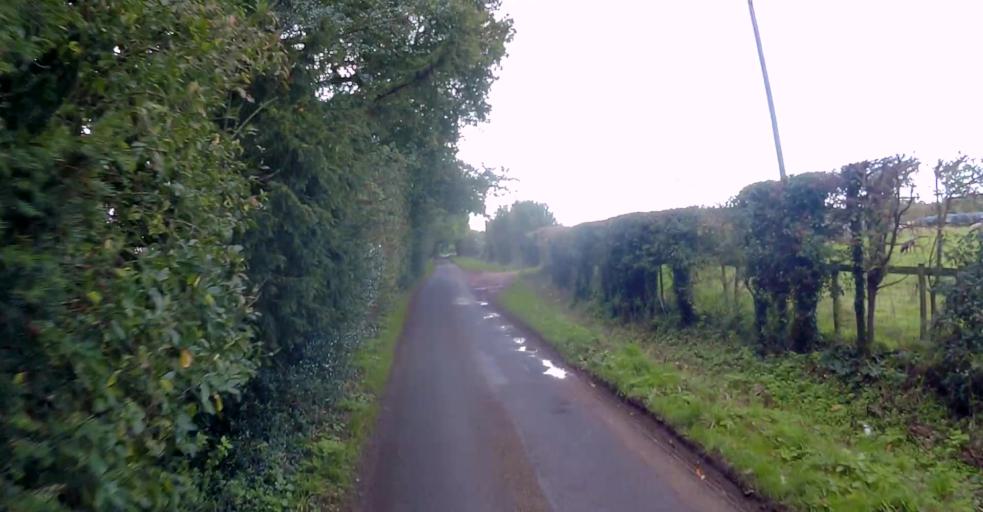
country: GB
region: England
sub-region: Surrey
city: Farnham
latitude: 51.2082
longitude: -0.8359
